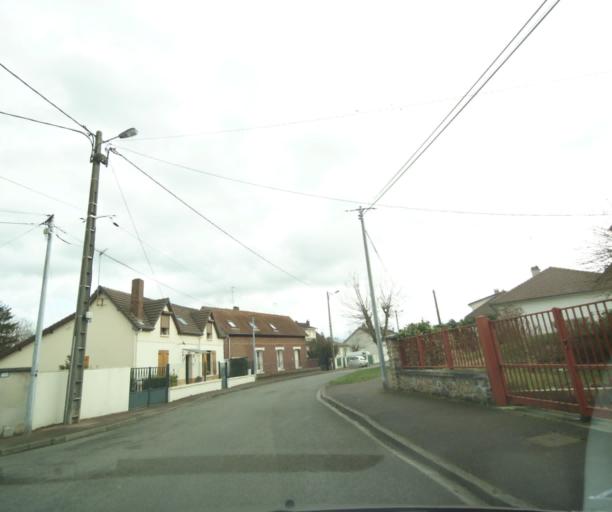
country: FR
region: Picardie
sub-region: Departement de l'Oise
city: Noyon
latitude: 49.5825
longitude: 2.9900
